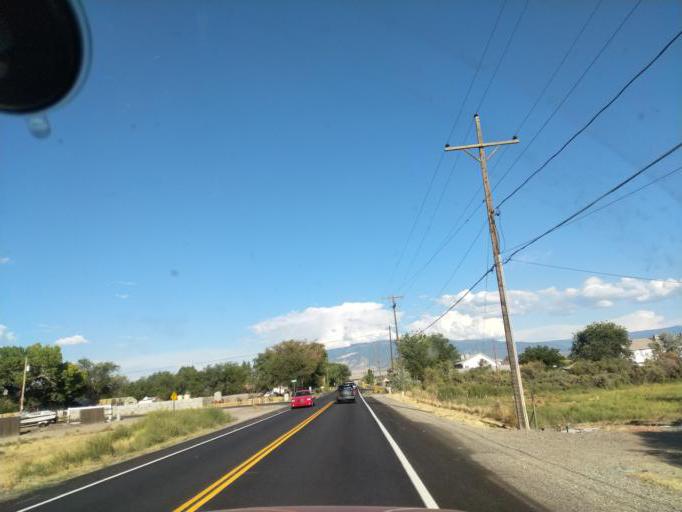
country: US
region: Colorado
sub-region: Mesa County
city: Fruitvale
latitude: 39.0628
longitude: -108.4789
